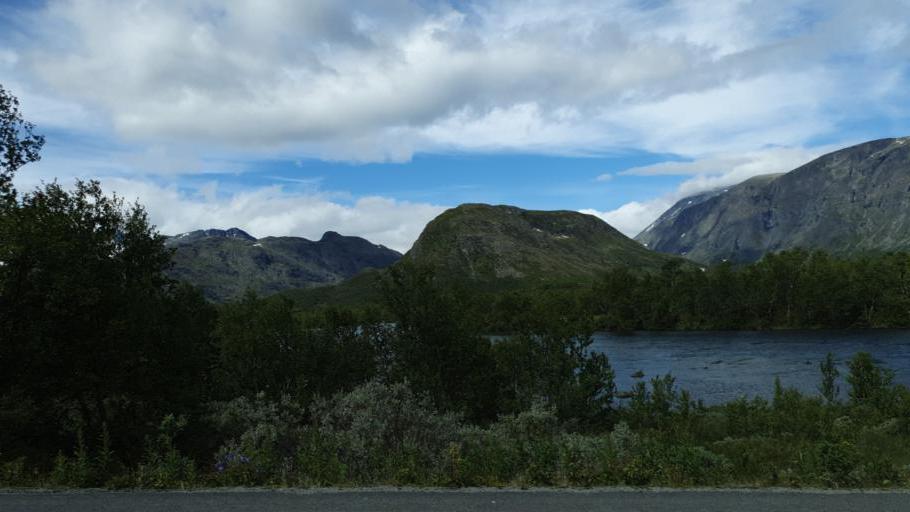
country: NO
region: Oppland
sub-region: Oystre Slidre
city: Heggenes
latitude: 61.4839
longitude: 8.8372
